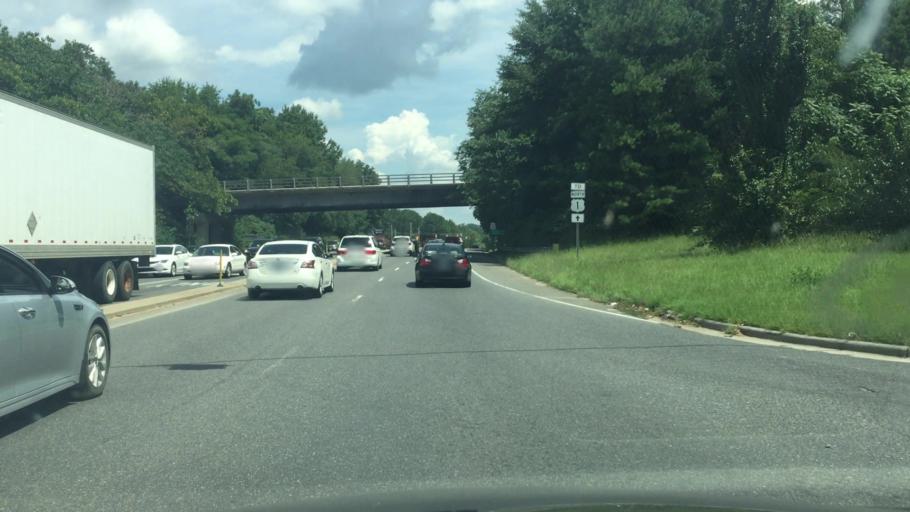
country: US
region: North Carolina
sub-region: Richmond County
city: Rockingham
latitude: 34.9380
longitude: -79.7792
